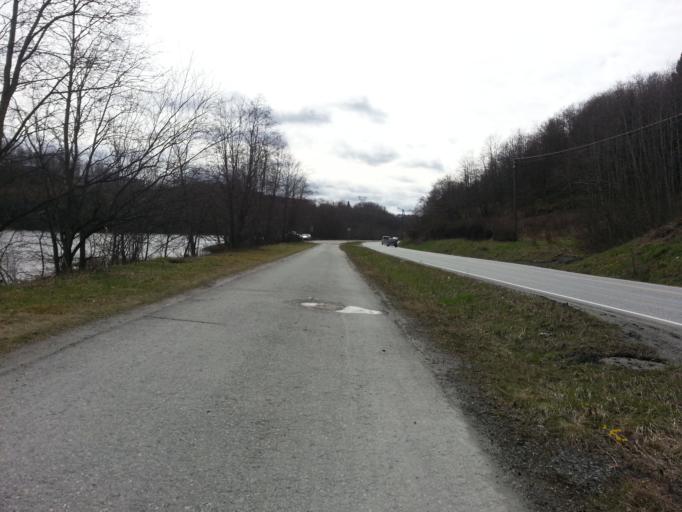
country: NO
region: Sor-Trondelag
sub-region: Trondheim
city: Trondheim
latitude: 63.4011
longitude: 10.3885
